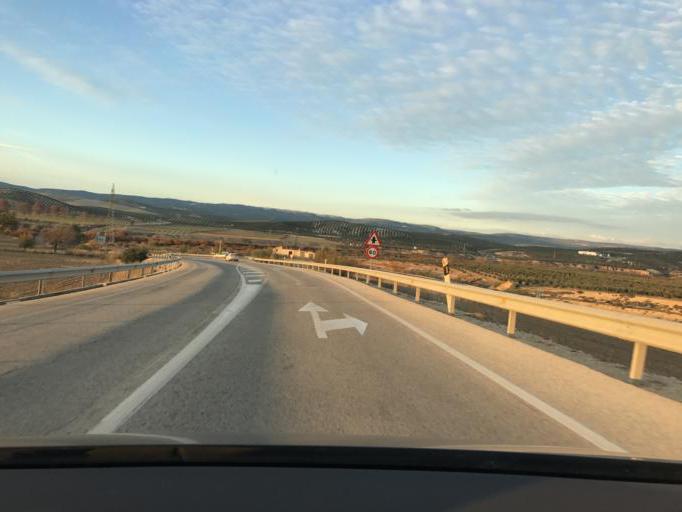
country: ES
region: Andalusia
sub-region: Provincia de Jaen
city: Jodar
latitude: 37.9140
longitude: -3.3470
